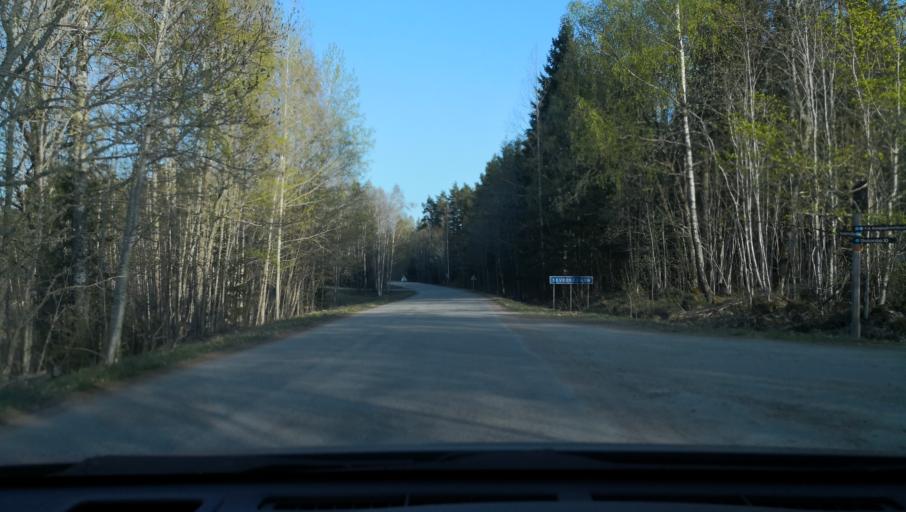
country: SE
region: Uppsala
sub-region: Heby Kommun
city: Tarnsjo
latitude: 60.2669
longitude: 16.9159
